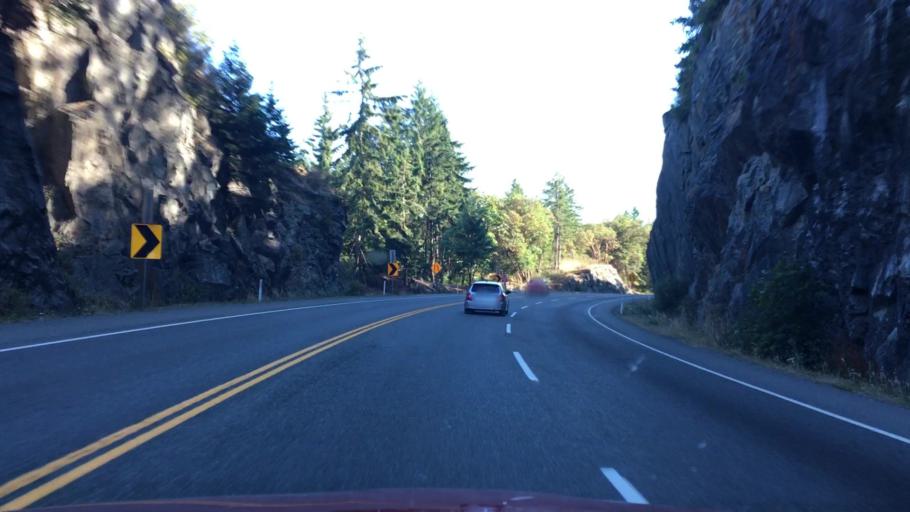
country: CA
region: British Columbia
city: North Saanich
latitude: 48.5846
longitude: -123.5299
